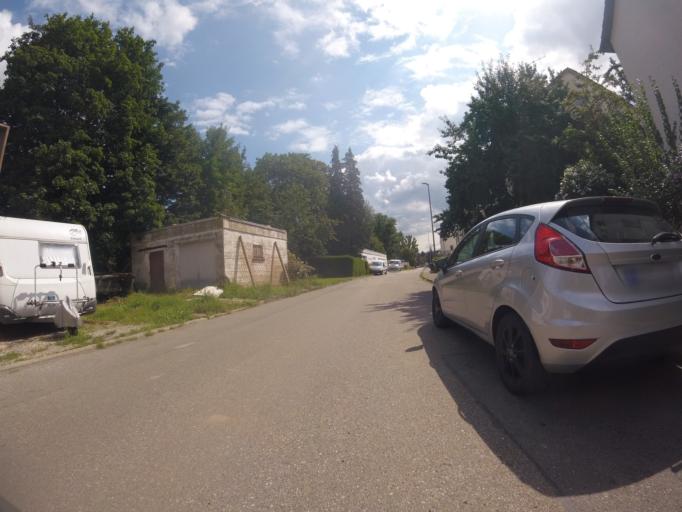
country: DE
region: Baden-Wuerttemberg
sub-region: Regierungsbezirk Stuttgart
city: Winterbach
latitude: 48.8031
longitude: 9.4741
